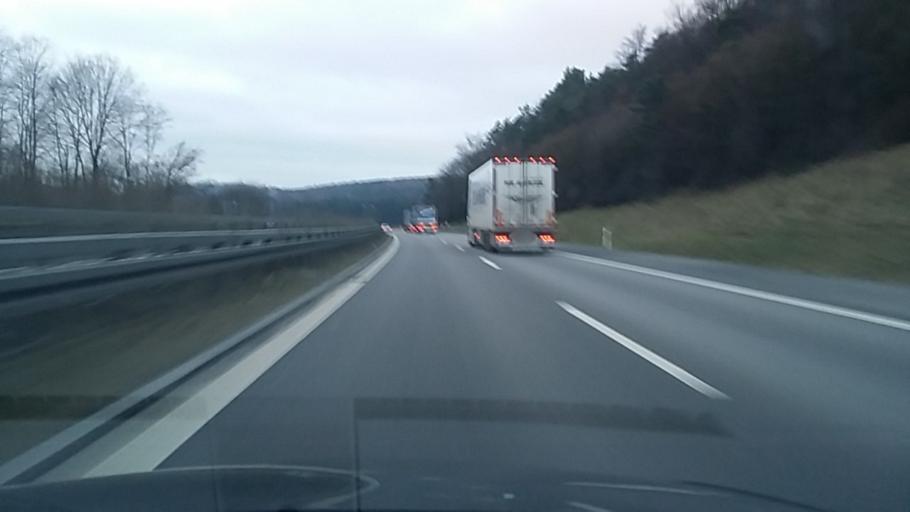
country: DE
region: Bavaria
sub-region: Upper Palatinate
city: Velburg
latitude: 49.1965
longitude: 11.6800
